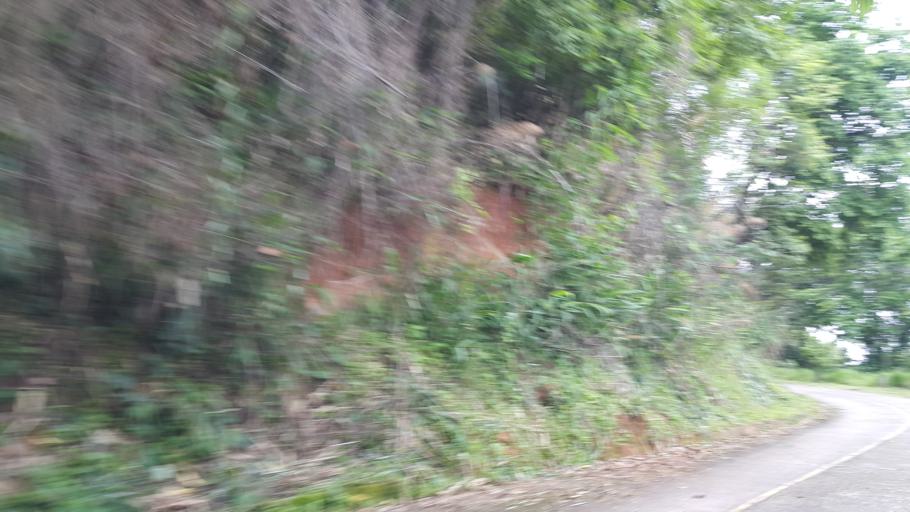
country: TH
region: Lampang
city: Mueang Pan
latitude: 18.8280
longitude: 99.3927
